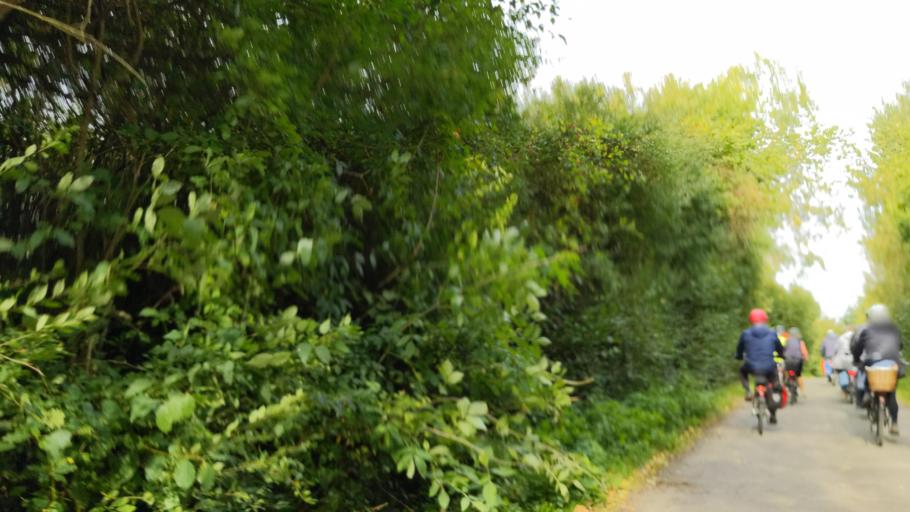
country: DE
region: Schleswig-Holstein
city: Mechow
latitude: 53.7287
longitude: 10.8060
